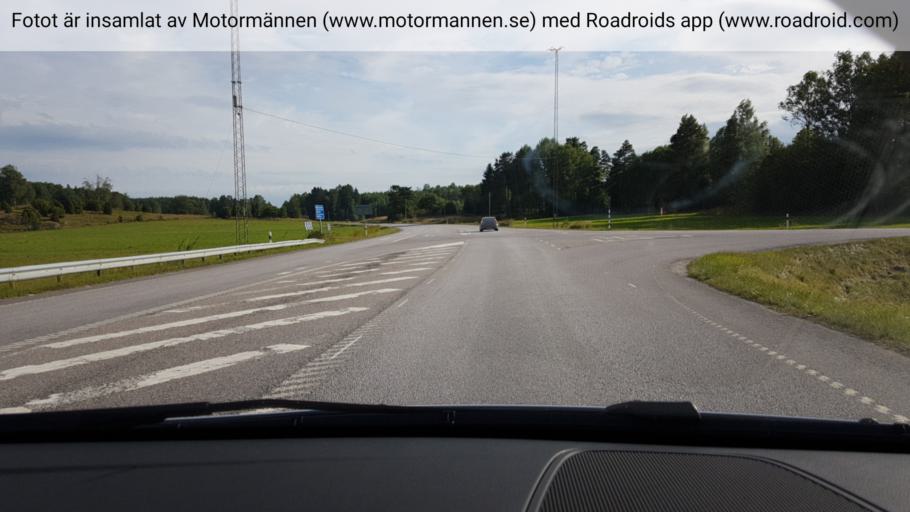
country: SE
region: Stockholm
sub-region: Norrtalje Kommun
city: Norrtalje
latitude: 59.8819
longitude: 18.6989
